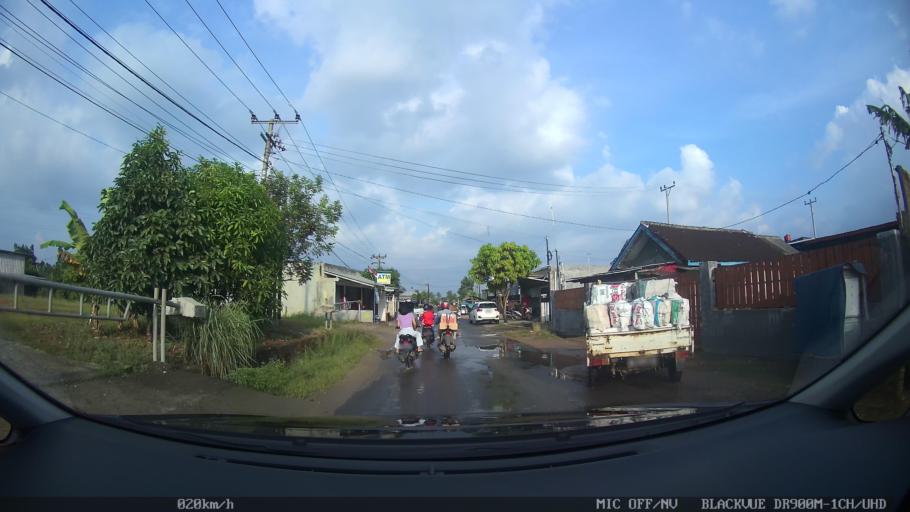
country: ID
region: Lampung
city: Kedaton
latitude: -5.3882
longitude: 105.3182
